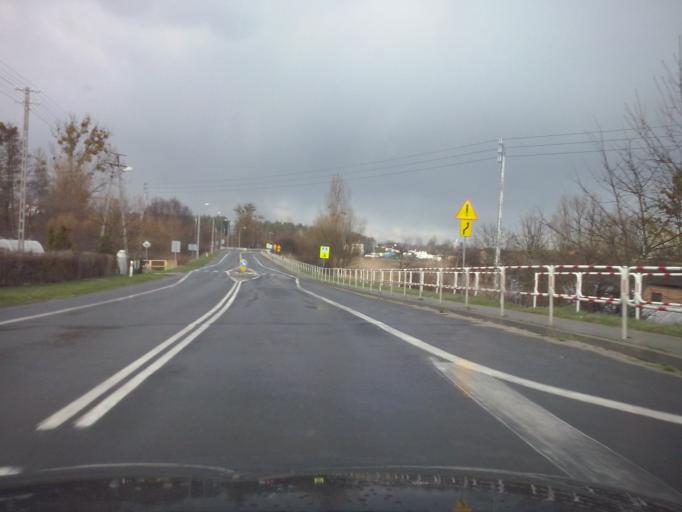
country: PL
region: Lublin Voivodeship
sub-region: Powiat krasnostawski
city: Krasnystaw
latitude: 51.0126
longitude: 23.1914
